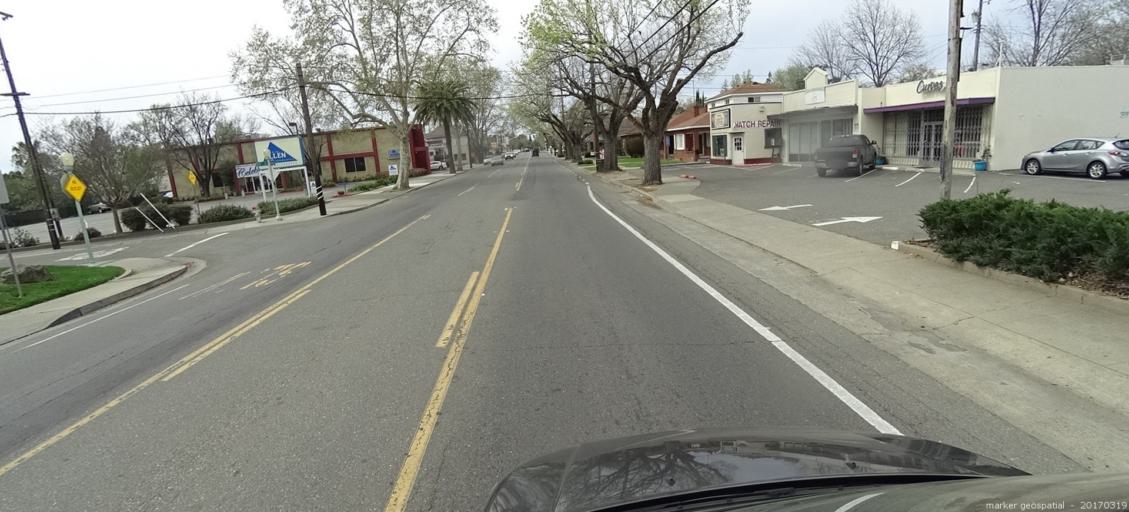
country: US
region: California
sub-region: Sacramento County
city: Sacramento
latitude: 38.5597
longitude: -121.4413
